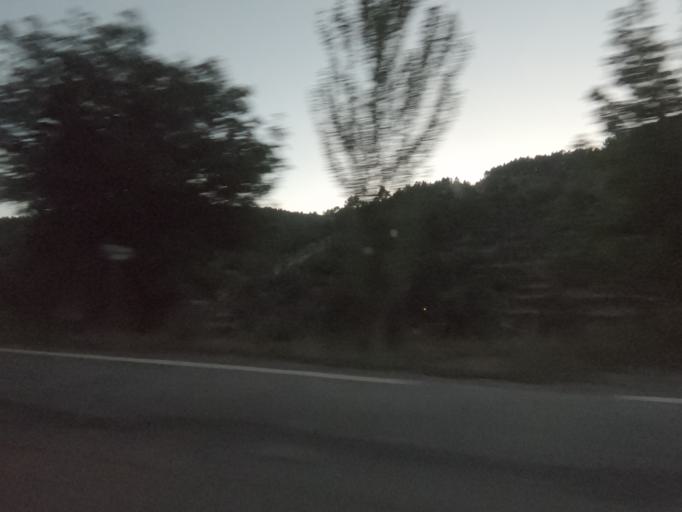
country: PT
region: Vila Real
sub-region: Vila Real
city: Vila Real
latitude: 41.2515
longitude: -7.6882
